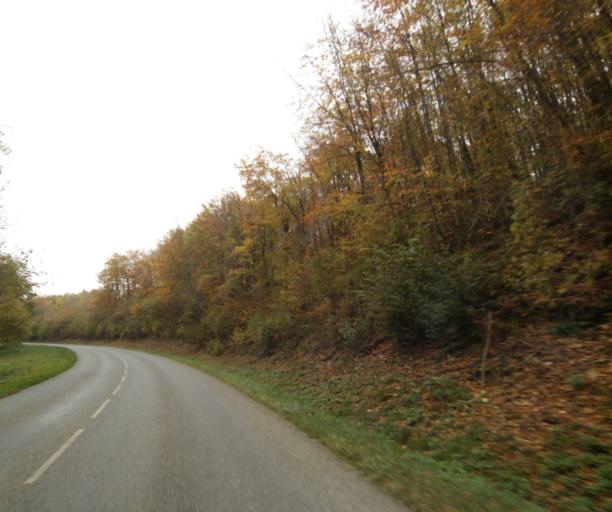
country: FR
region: Lorraine
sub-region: Departement de Meurthe-et-Moselle
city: Joeuf
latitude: 49.2535
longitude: 6.0147
